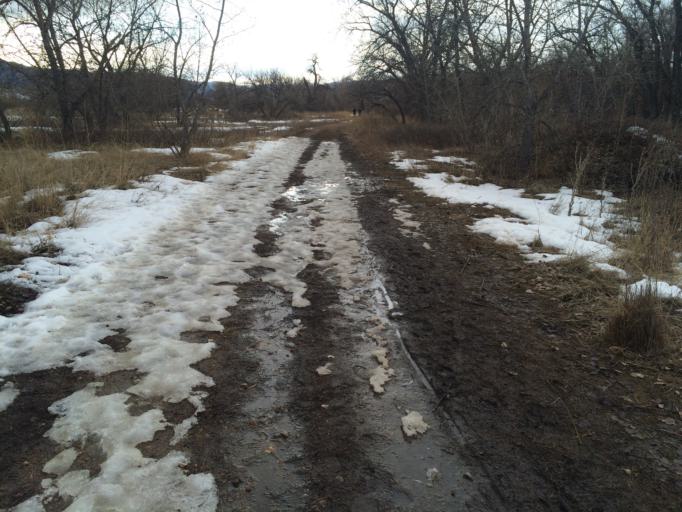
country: US
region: Colorado
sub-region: Boulder County
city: Gunbarrel
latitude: 40.0395
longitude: -105.1943
